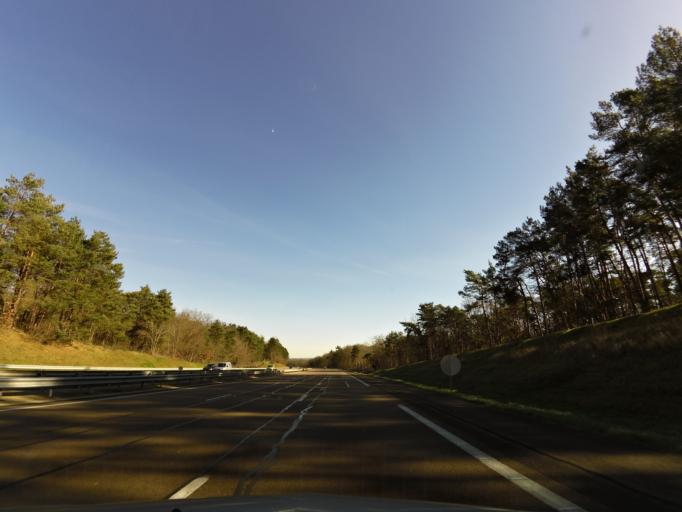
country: FR
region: Bourgogne
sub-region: Departement de l'Yonne
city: Appoigny
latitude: 47.8657
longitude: 3.4981
